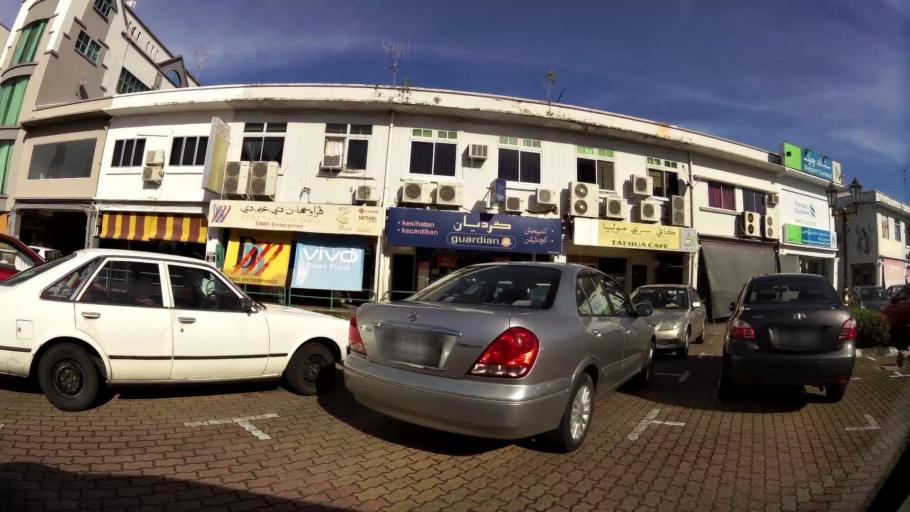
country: BN
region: Belait
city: Kuala Belait
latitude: 4.5829
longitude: 114.1918
